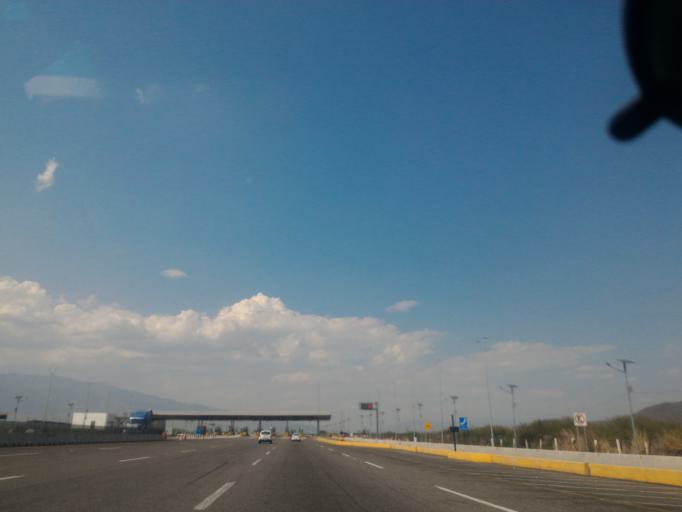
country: MX
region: Jalisco
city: Usmajac
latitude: 19.9311
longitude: -103.5295
